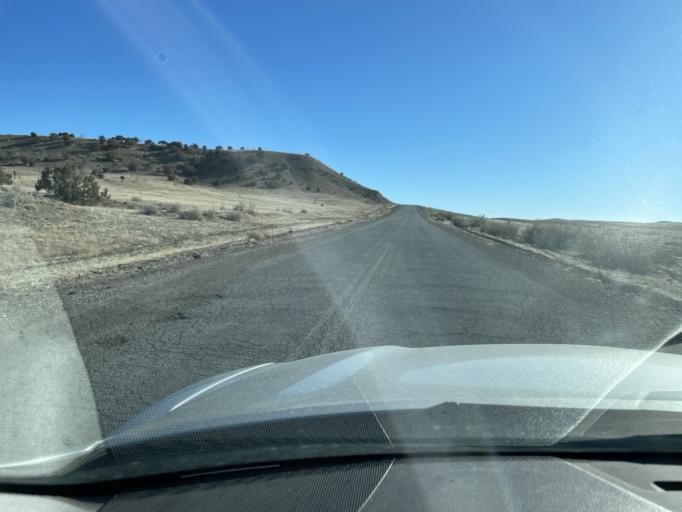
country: US
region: Colorado
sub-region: Mesa County
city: Loma
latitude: 39.1993
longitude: -109.1212
